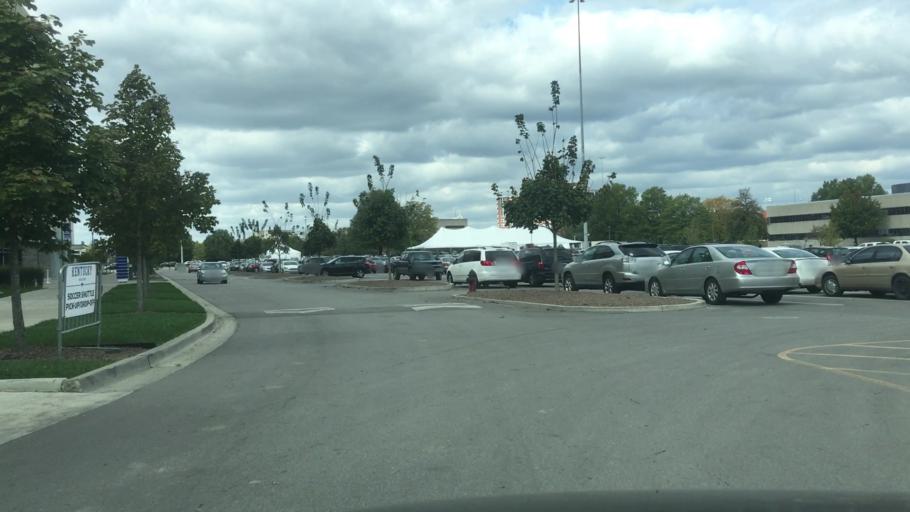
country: US
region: Kentucky
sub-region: Fayette County
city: Mount Vernon
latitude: 38.0233
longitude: -84.5036
